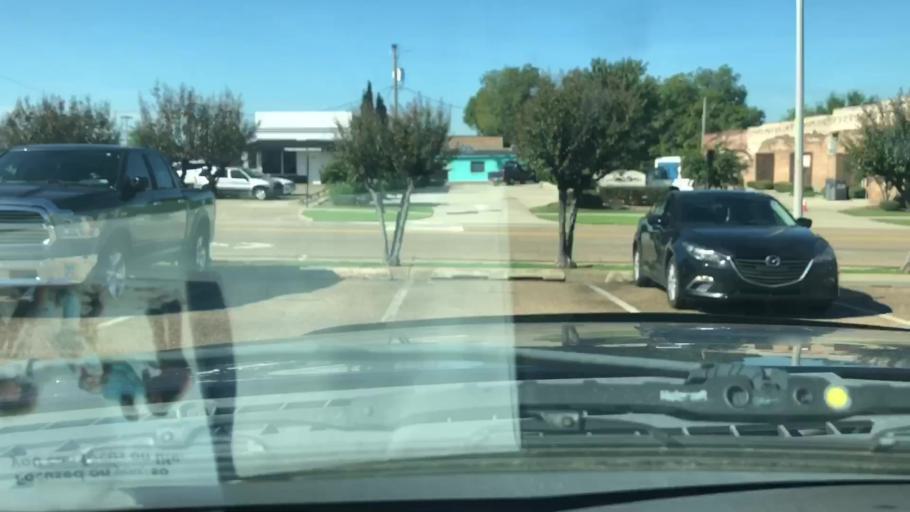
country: US
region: Texas
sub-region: Bowie County
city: Texarkana
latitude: 33.4218
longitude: -94.0457
